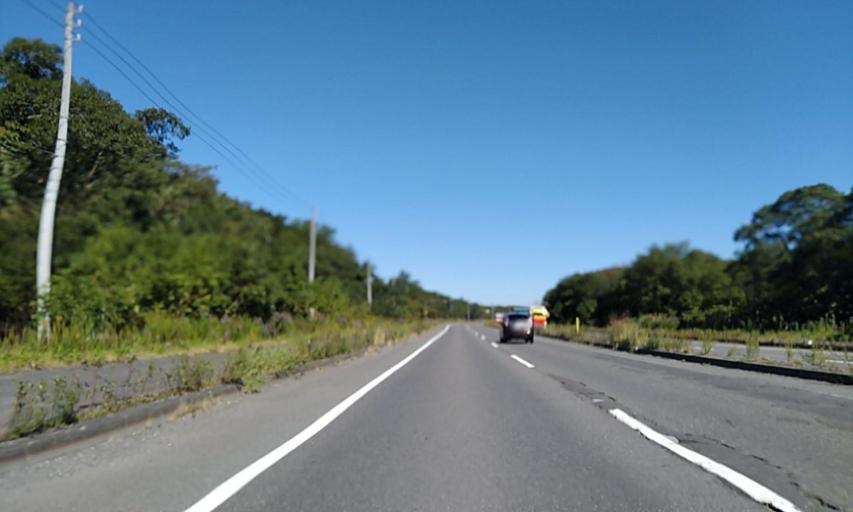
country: JP
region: Hokkaido
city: Chitose
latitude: 42.7279
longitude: 141.7090
